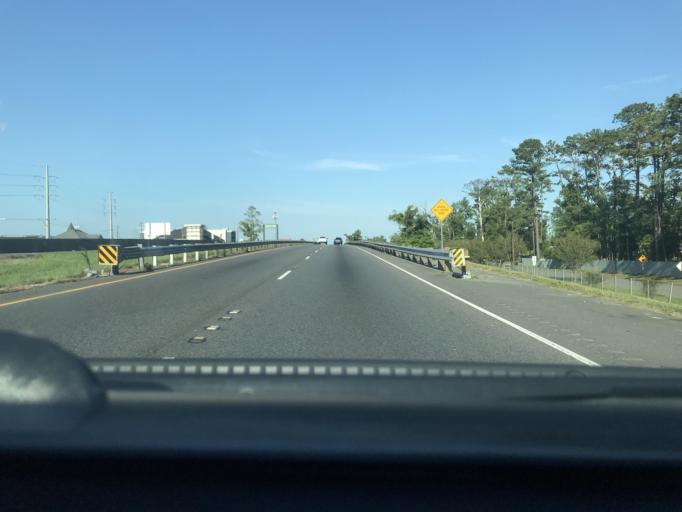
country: US
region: Louisiana
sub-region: Calcasieu Parish
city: Prien
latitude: 30.1968
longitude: -93.2428
